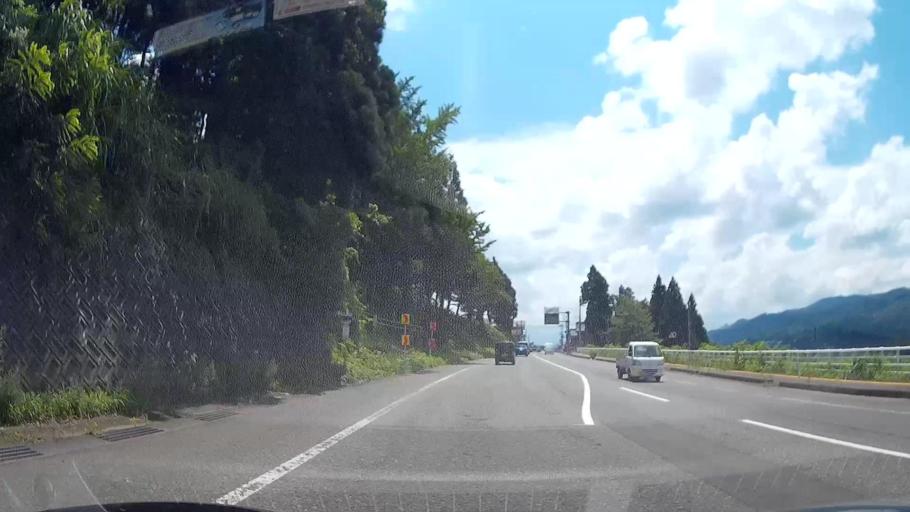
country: JP
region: Niigata
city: Tokamachi
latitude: 37.0816
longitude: 138.7216
